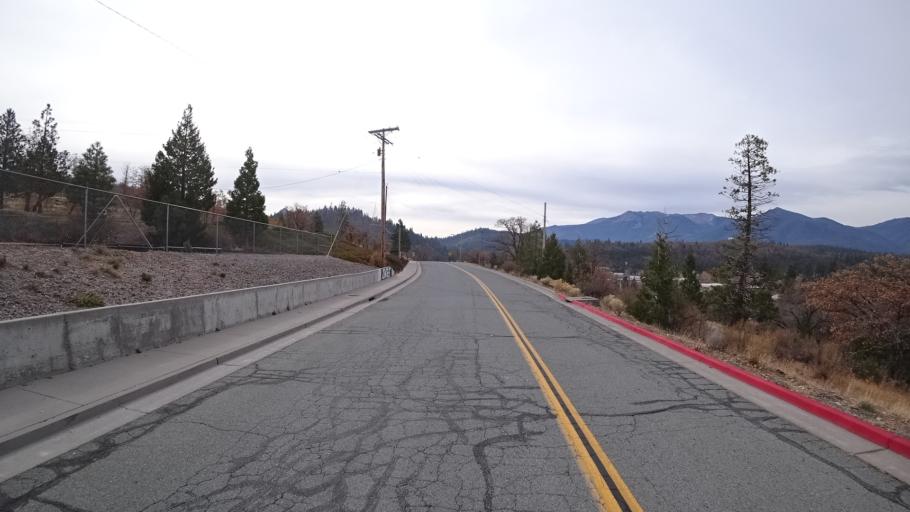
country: US
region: California
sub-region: Siskiyou County
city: Weed
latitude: 41.4270
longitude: -122.3814
